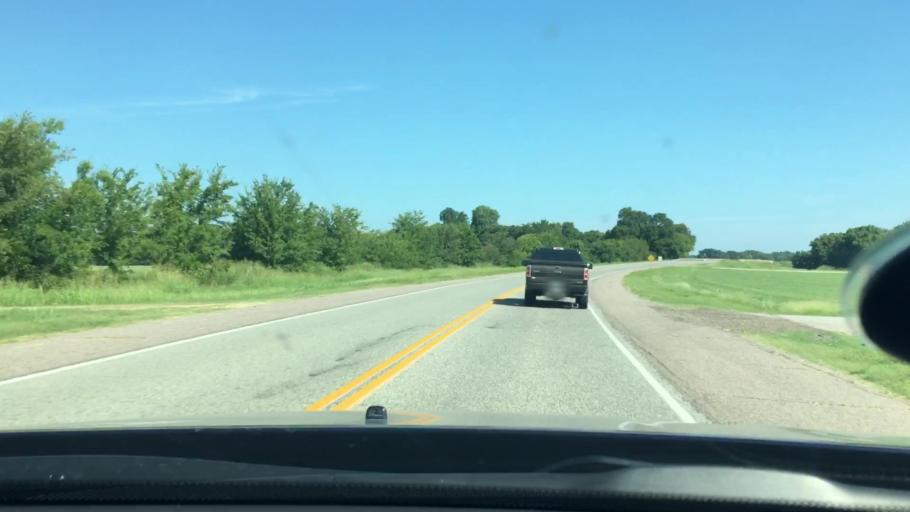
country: US
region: Oklahoma
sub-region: Johnston County
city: Tishomingo
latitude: 34.2473
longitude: -96.5492
